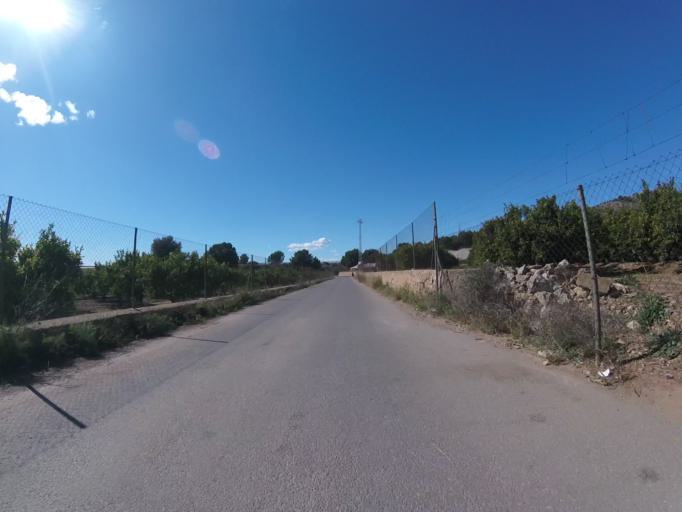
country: ES
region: Valencia
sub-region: Provincia de Castello
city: Benicassim
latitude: 40.0665
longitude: 0.0732
